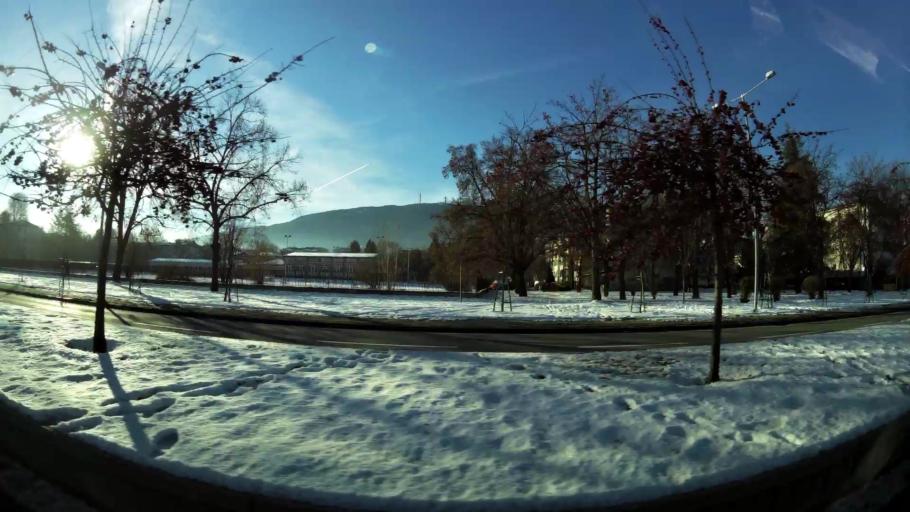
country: MK
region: Karpos
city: Skopje
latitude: 42.0075
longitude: 21.3979
